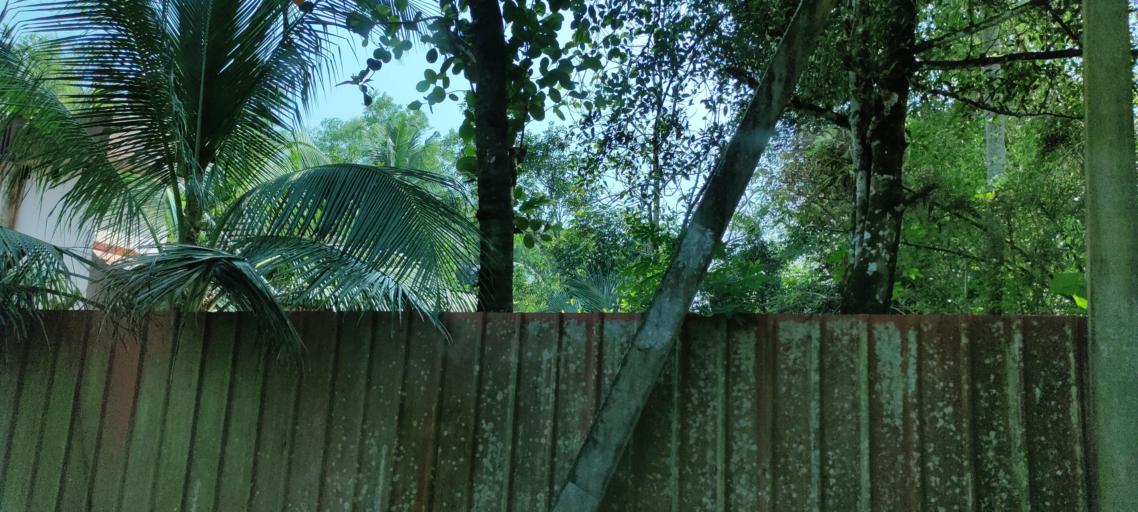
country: IN
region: Kerala
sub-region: Alappuzha
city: Shertallai
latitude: 9.6034
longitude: 76.3200
